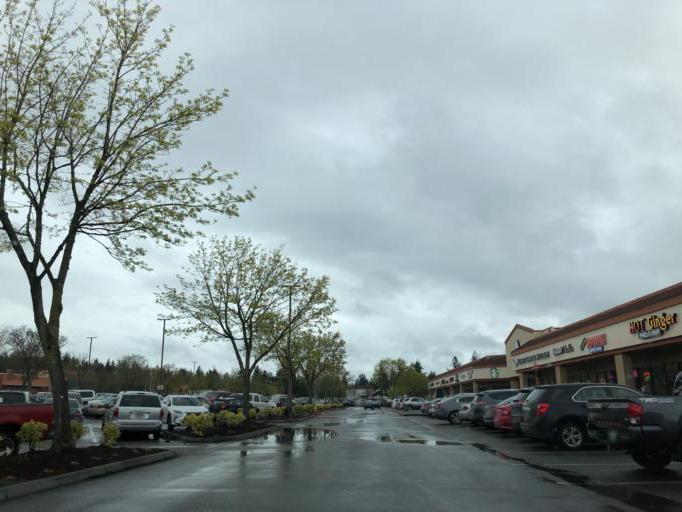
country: US
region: Washington
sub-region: Thurston County
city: Tanglewilde-Thompson Place
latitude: 47.0601
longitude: -122.7661
